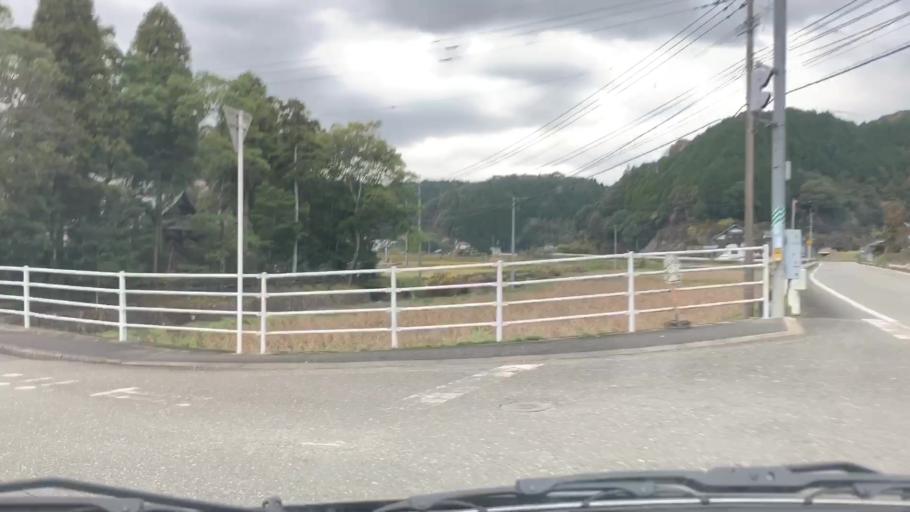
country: JP
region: Saga Prefecture
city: Ureshinomachi-shimojuku
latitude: 33.1380
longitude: 129.9718
